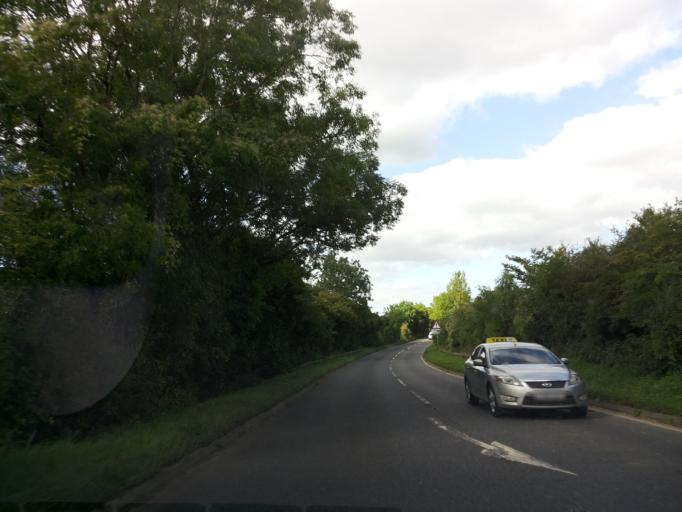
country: GB
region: England
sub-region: Bath and North East Somerset
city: Hinton Charterhouse
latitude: 51.3135
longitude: -2.3081
